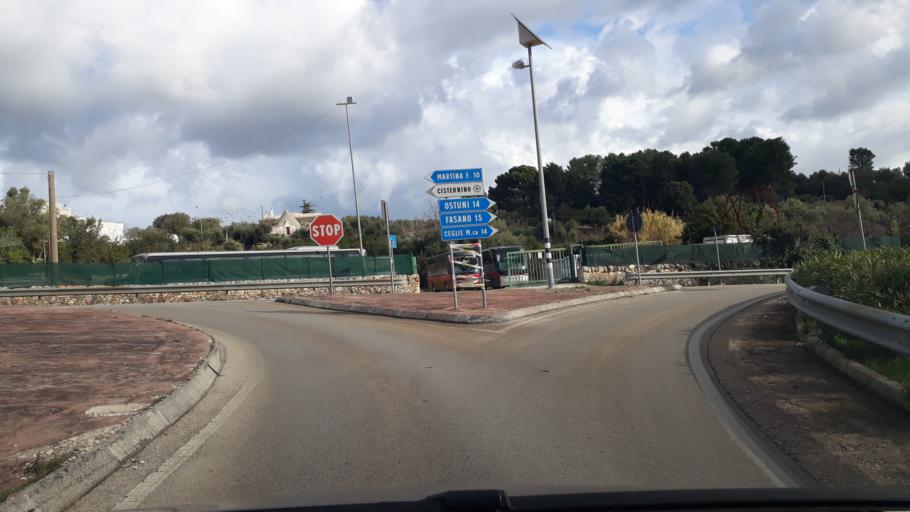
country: IT
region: Apulia
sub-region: Provincia di Brindisi
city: Cisternino
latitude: 40.7377
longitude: 17.4300
